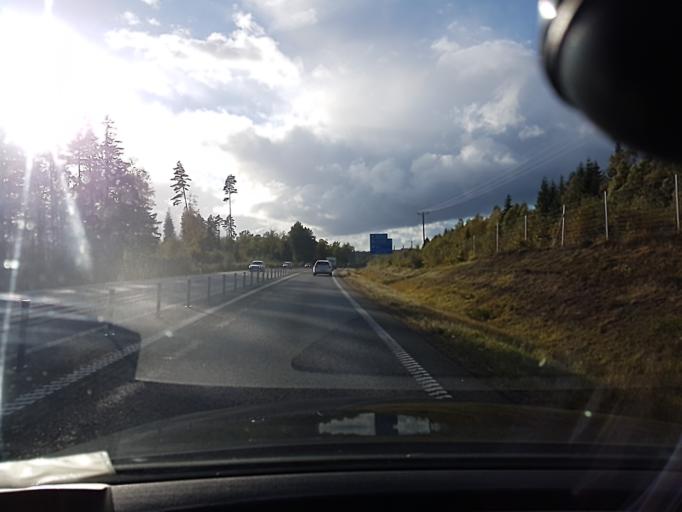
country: SE
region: Kronoberg
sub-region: Ljungby Kommun
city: Ljungby
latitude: 56.8495
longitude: 13.9847
